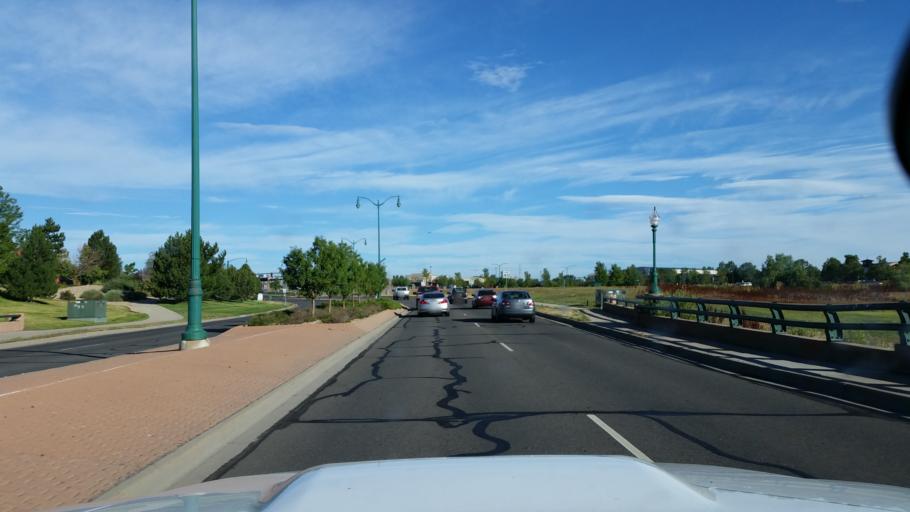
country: US
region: Colorado
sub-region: Broomfield County
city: Broomfield
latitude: 39.8871
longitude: -105.0650
